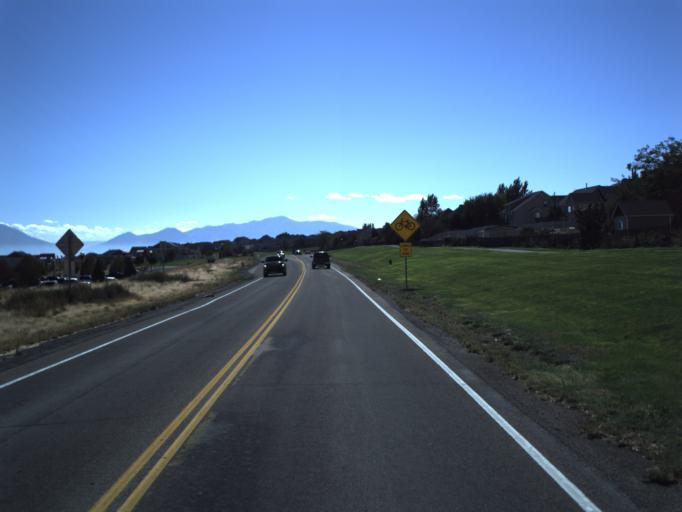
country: US
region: Utah
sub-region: Utah County
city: Saratoga Springs
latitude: 40.3229
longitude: -111.9030
